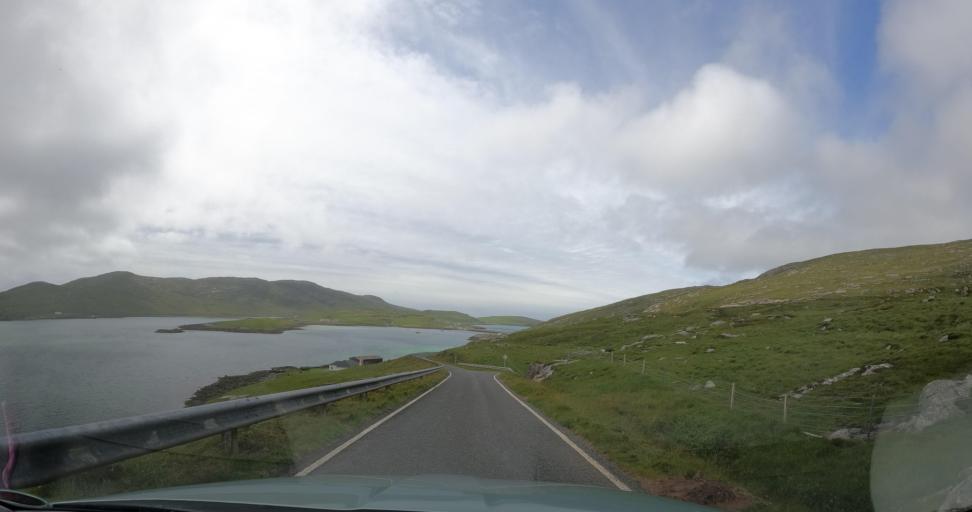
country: GB
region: Scotland
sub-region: Eilean Siar
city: Barra
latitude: 56.9487
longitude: -7.5149
